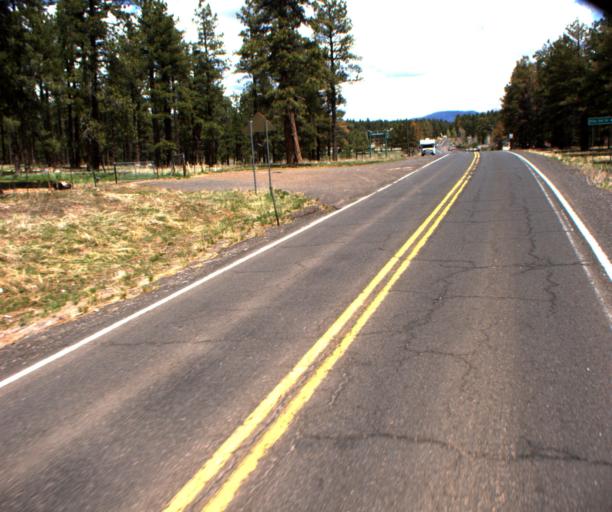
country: US
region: Arizona
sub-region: Coconino County
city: Kachina Village
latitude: 35.1256
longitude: -111.6930
